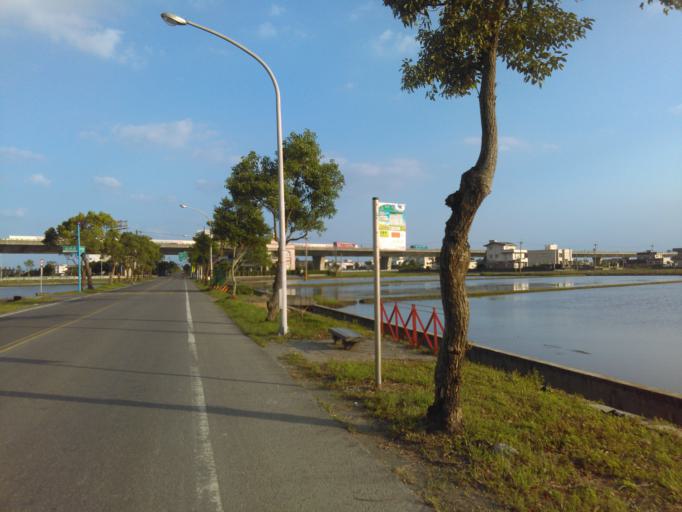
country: TW
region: Taiwan
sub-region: Yilan
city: Yilan
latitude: 24.8018
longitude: 121.7806
